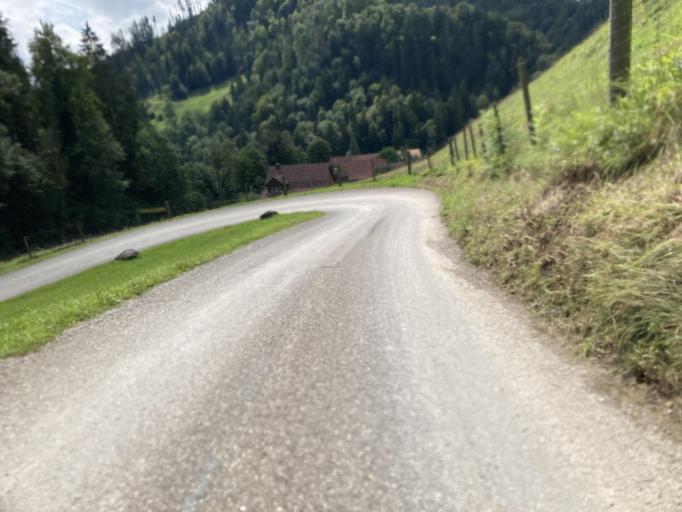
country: CH
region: Zurich
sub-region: Bezirk Pfaeffikon
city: Bauma
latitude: 47.3569
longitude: 8.9352
